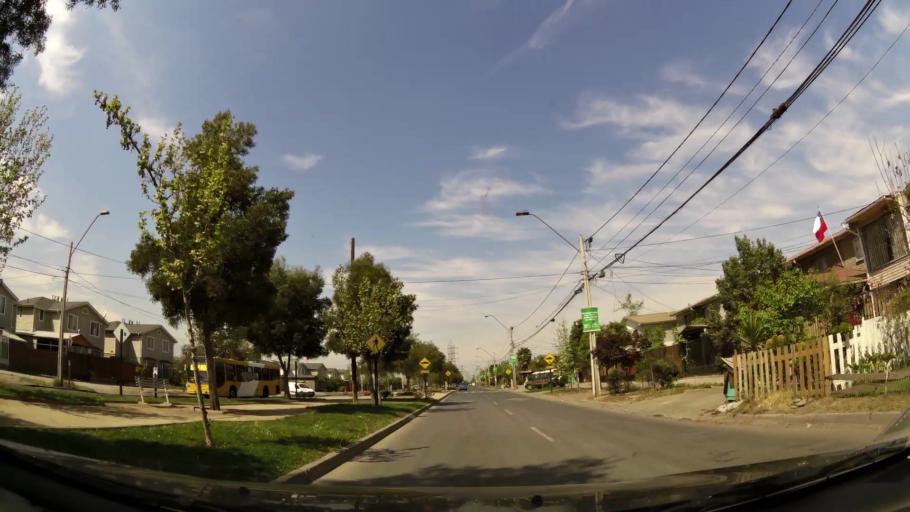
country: CL
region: Santiago Metropolitan
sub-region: Provincia de Santiago
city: La Pintana
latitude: -33.5736
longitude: -70.5993
